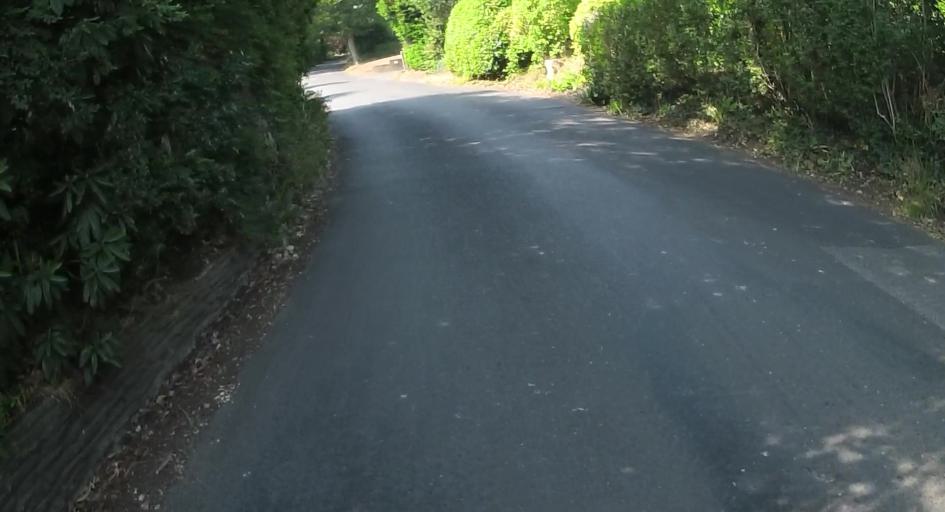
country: GB
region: England
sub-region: Surrey
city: Farnham
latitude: 51.1974
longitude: -0.8048
